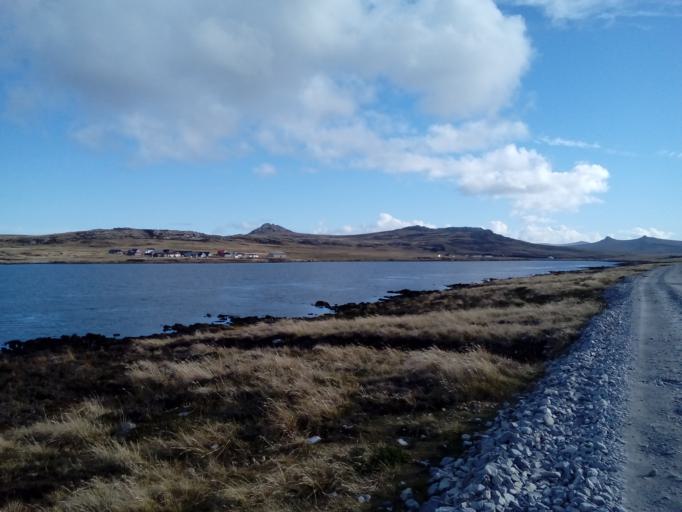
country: FK
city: Stanley
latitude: -51.6844
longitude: -57.8979
